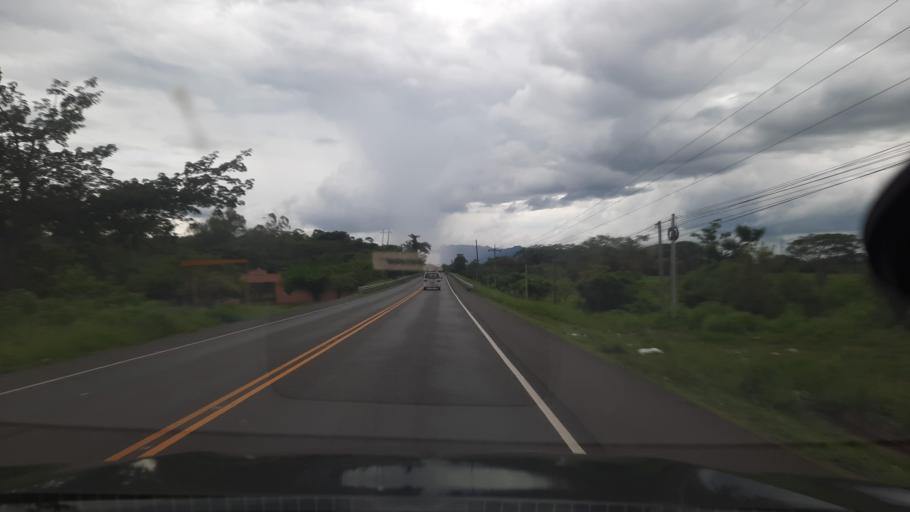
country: HN
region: Choluteca
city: Ciudad Choluteca
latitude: 13.3388
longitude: -87.2445
